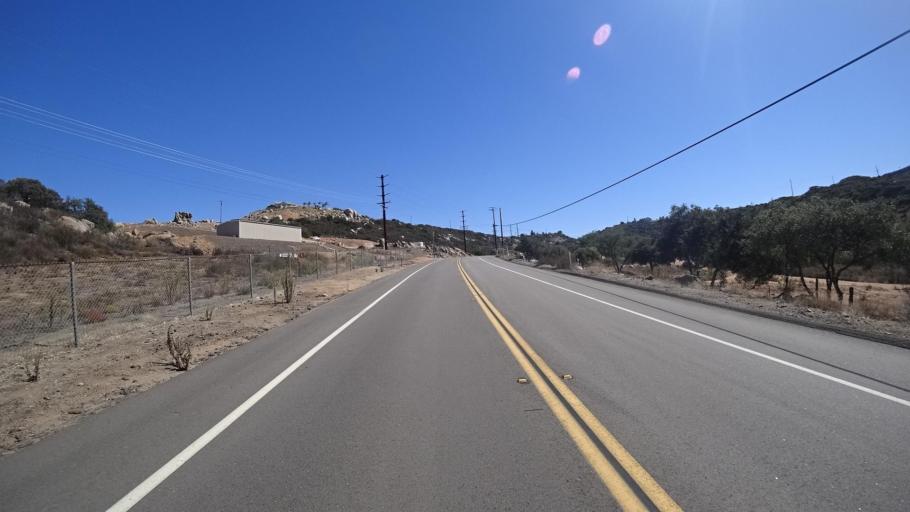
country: US
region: California
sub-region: San Diego County
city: Alpine
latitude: 32.7708
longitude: -116.7005
